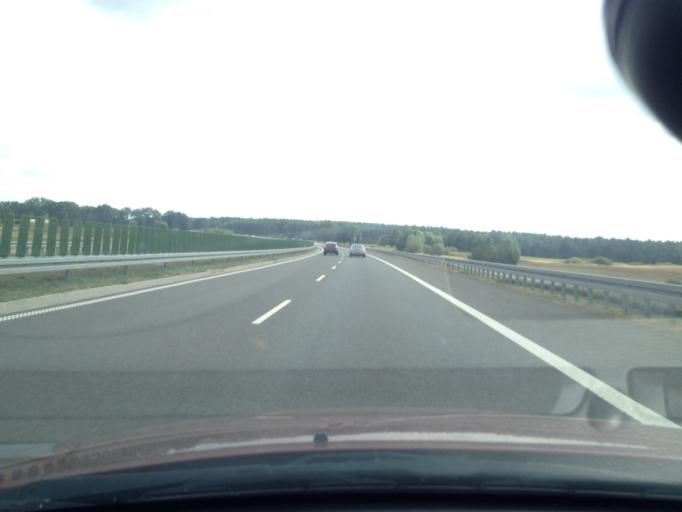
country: PL
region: West Pomeranian Voivodeship
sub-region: Powiat pyrzycki
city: Bielice
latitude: 53.1764
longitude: 14.6921
